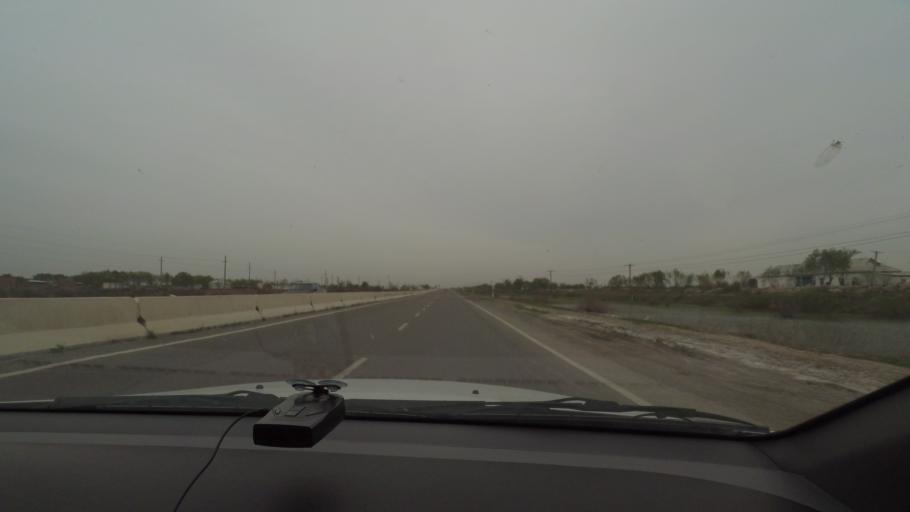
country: UZ
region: Sirdaryo
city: Guliston
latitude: 40.4964
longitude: 68.6192
